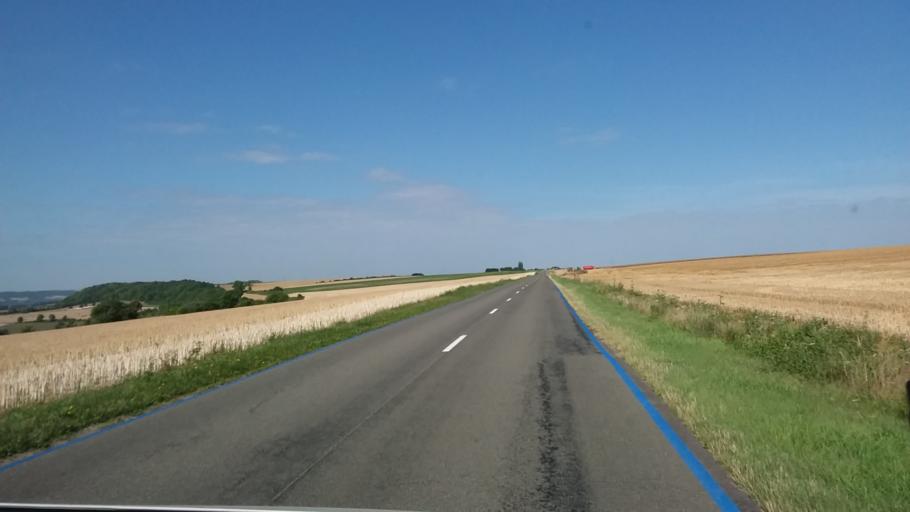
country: FR
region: Picardie
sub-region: Departement de l'Aisne
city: Bruyeres-et-Montberault
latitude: 49.4409
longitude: 3.6924
